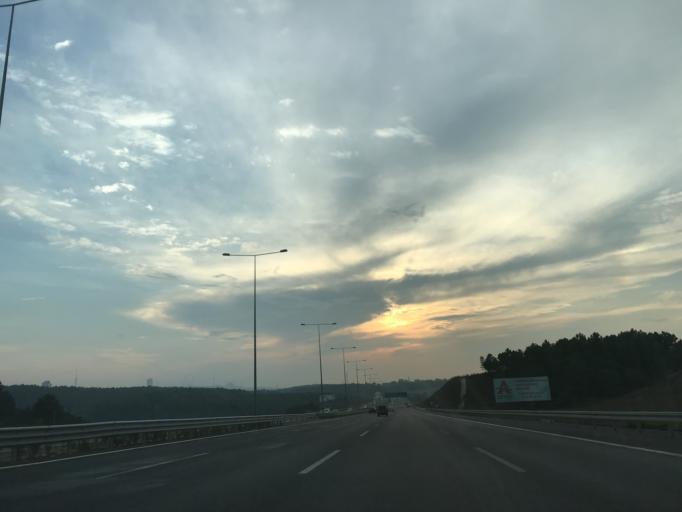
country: TR
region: Istanbul
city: Umraniye
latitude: 41.0495
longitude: 29.1438
